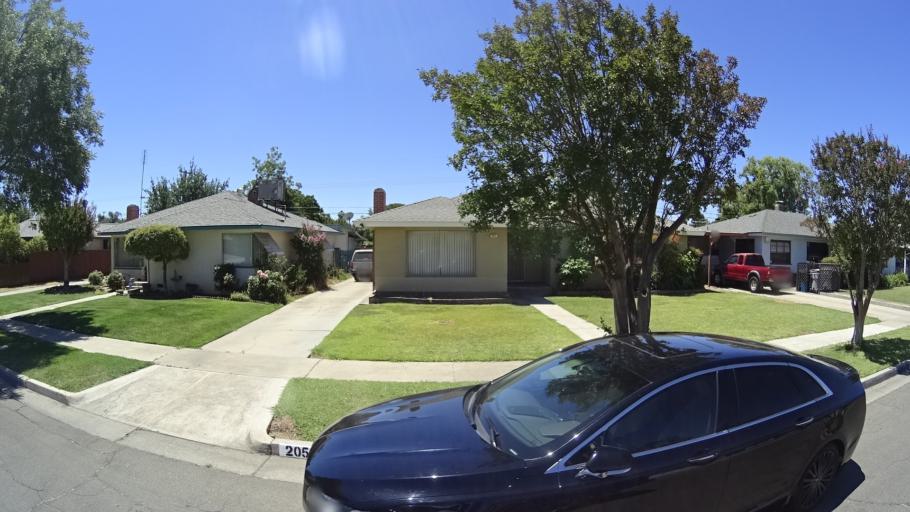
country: US
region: California
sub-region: Fresno County
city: Fresno
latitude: 36.7848
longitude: -119.8143
